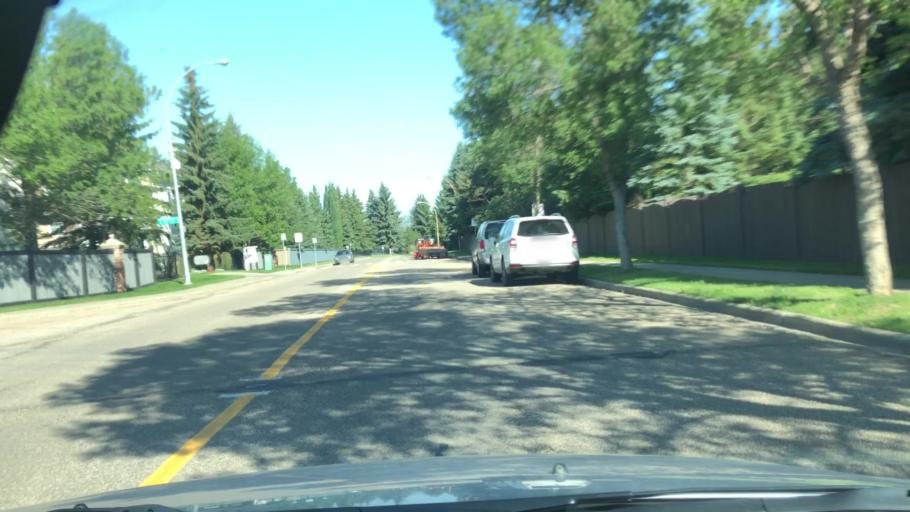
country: CA
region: Alberta
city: Edmonton
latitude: 53.4754
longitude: -113.6002
